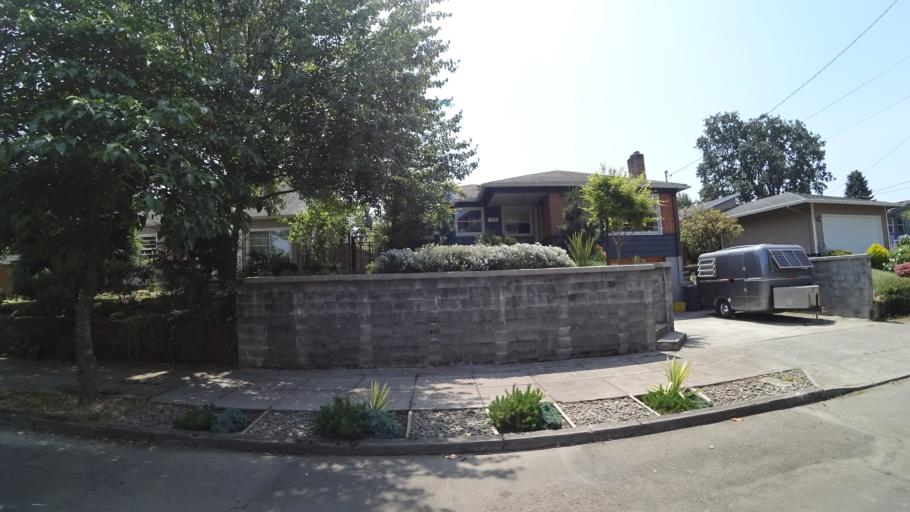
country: US
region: Oregon
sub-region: Multnomah County
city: Portland
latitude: 45.5807
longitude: -122.6731
